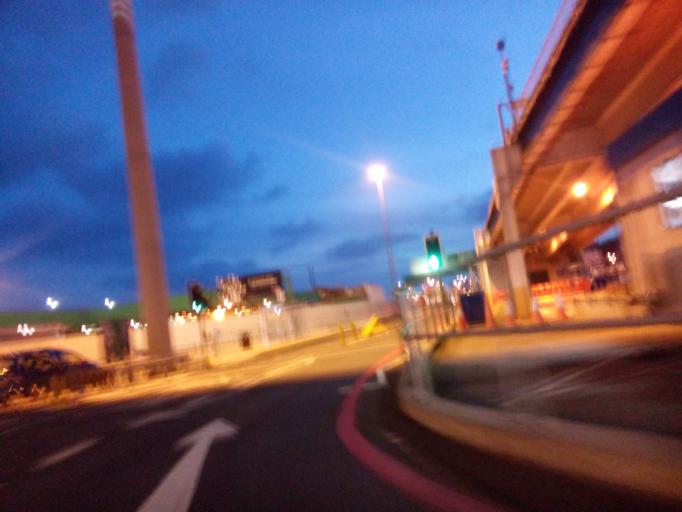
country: GB
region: England
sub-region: Kent
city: Dover
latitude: 51.1274
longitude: 1.3304
